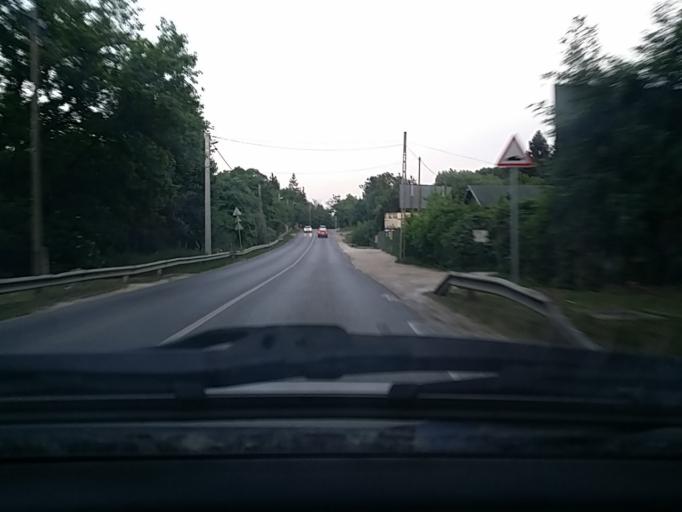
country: HU
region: Pest
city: Solymar
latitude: 47.5741
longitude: 18.9418
